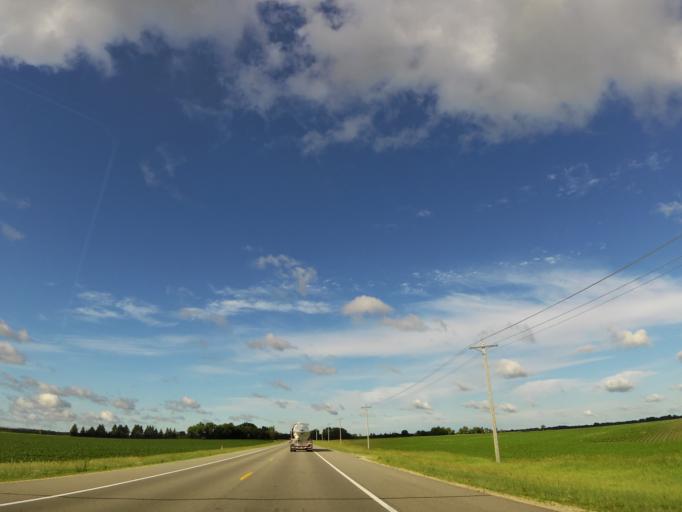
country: US
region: Minnesota
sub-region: Dakota County
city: Hastings
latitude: 44.6983
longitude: -92.8975
